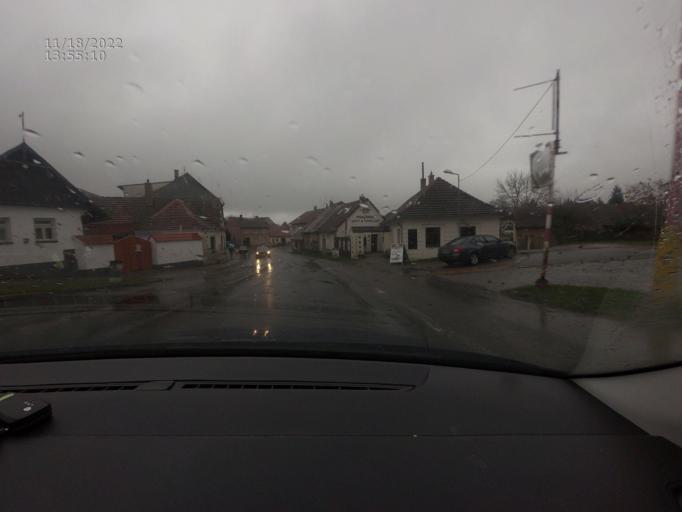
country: CZ
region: Jihocesky
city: Sedlice
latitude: 49.3782
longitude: 13.9371
